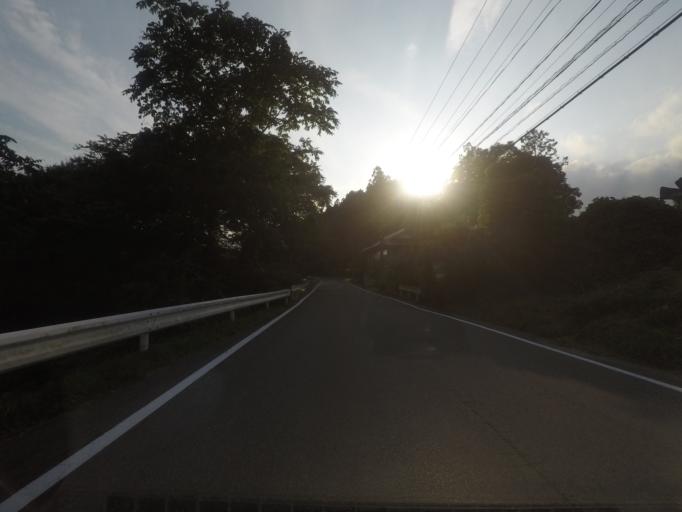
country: JP
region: Fukushima
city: Namie
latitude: 37.5661
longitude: 140.7974
